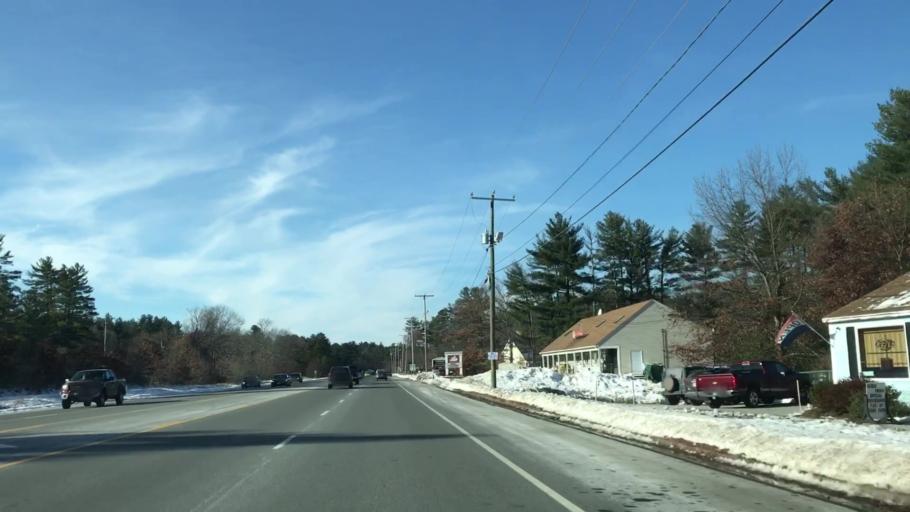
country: US
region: New Hampshire
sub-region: Hillsborough County
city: Milford
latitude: 42.8130
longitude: -71.5936
